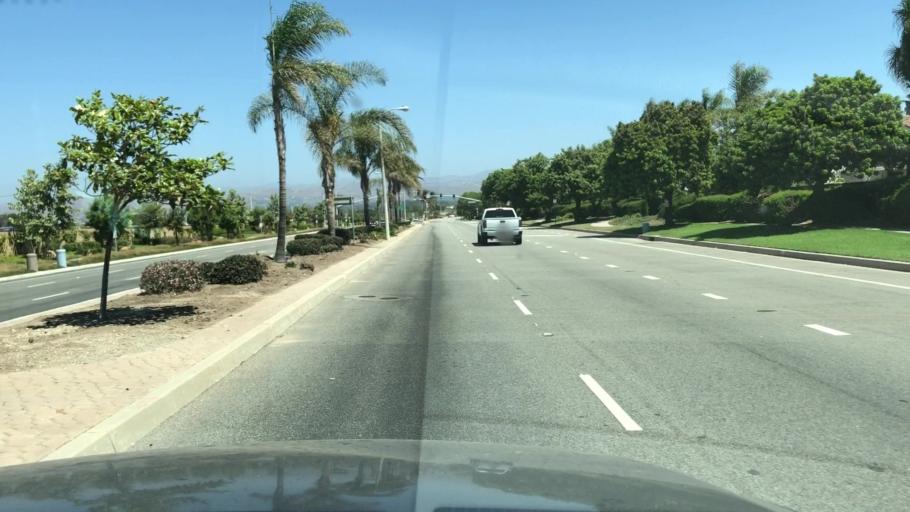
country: US
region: California
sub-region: Ventura County
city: El Rio
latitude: 34.2304
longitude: -119.1944
